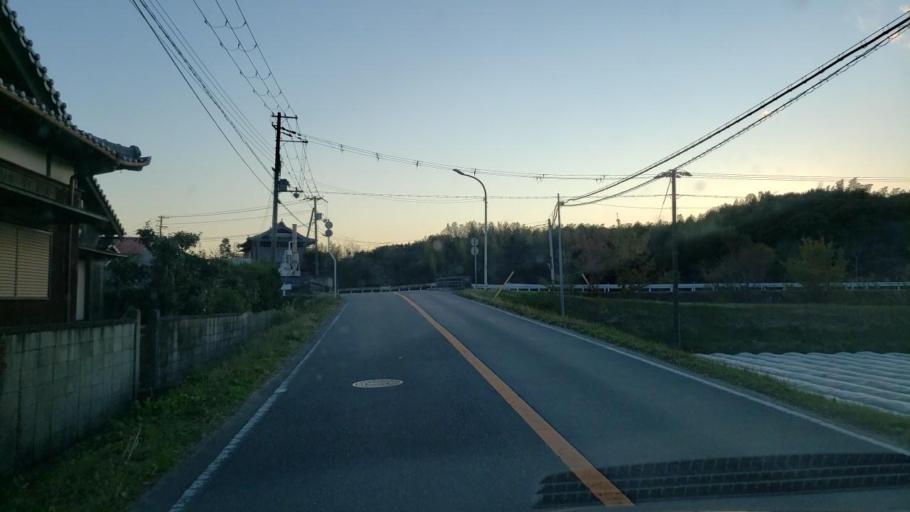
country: JP
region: Hyogo
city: Fukura
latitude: 34.3272
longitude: 134.7728
